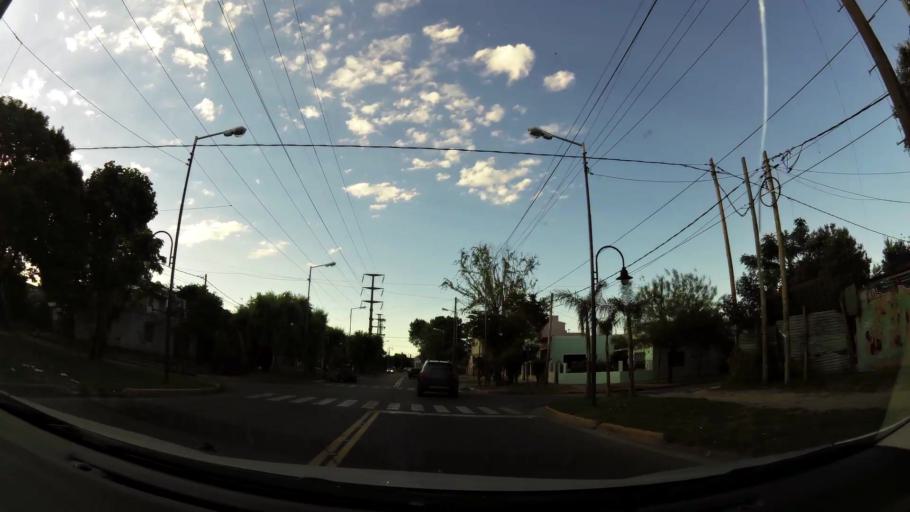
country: AR
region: Buenos Aires
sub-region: Partido de Tigre
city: Tigre
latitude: -34.4517
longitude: -58.5688
